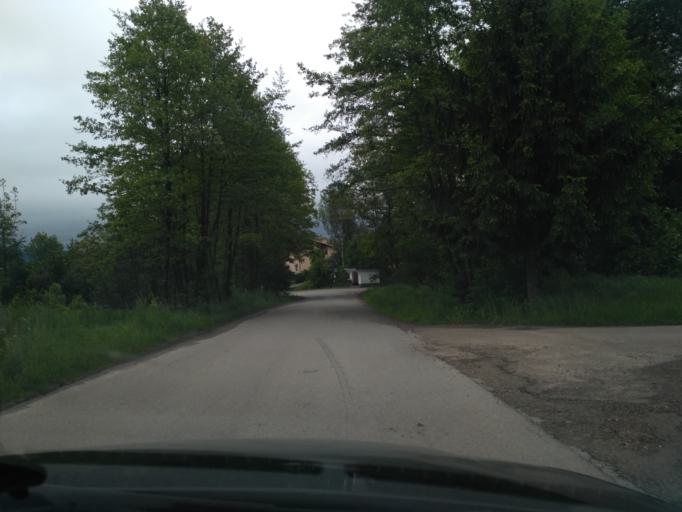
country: PL
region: Subcarpathian Voivodeship
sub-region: Powiat jasielski
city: Brzyska
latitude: 49.8198
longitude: 21.3617
